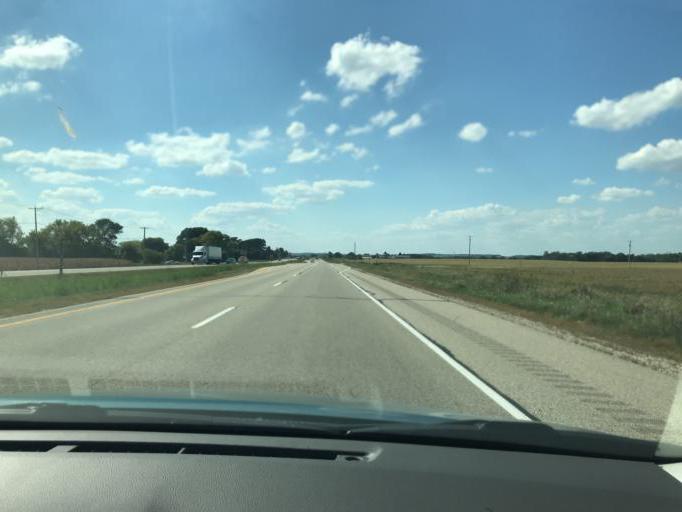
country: US
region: Wisconsin
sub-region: Walworth County
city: Pell Lake
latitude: 42.5967
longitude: -88.3621
